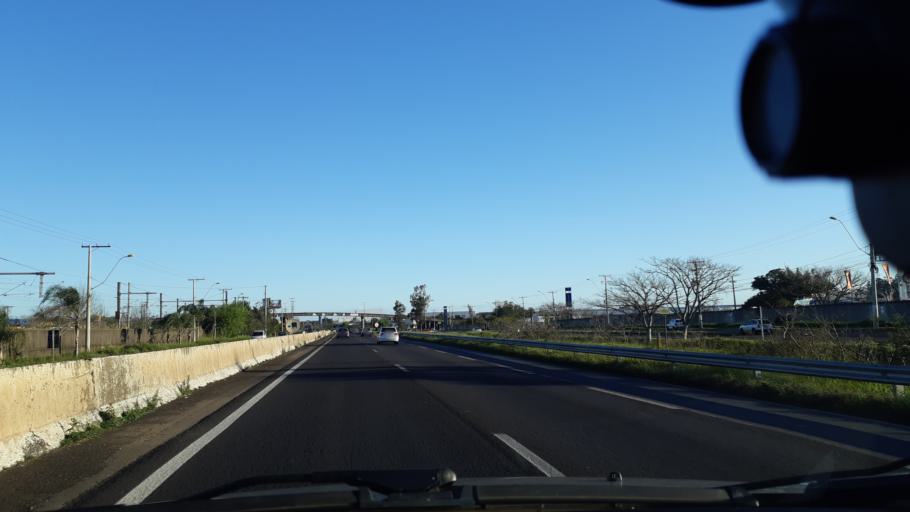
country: BR
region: Rio Grande do Sul
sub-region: Esteio
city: Esteio
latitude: -29.8564
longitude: -51.1804
